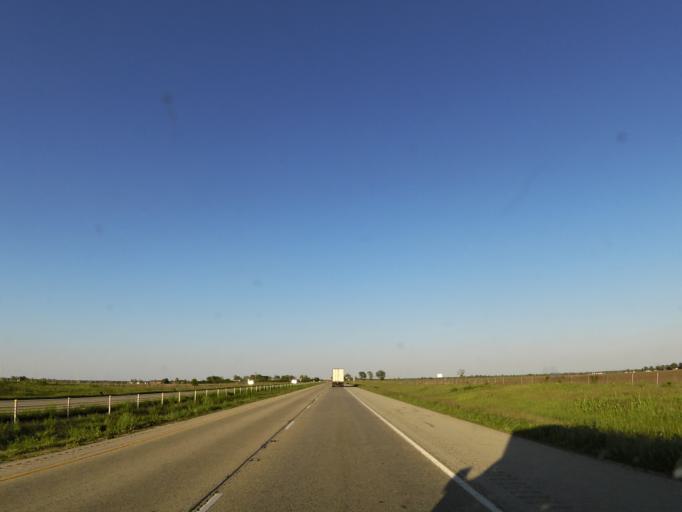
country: US
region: Illinois
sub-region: Vermilion County
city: Oakwood
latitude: 40.1248
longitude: -87.8248
